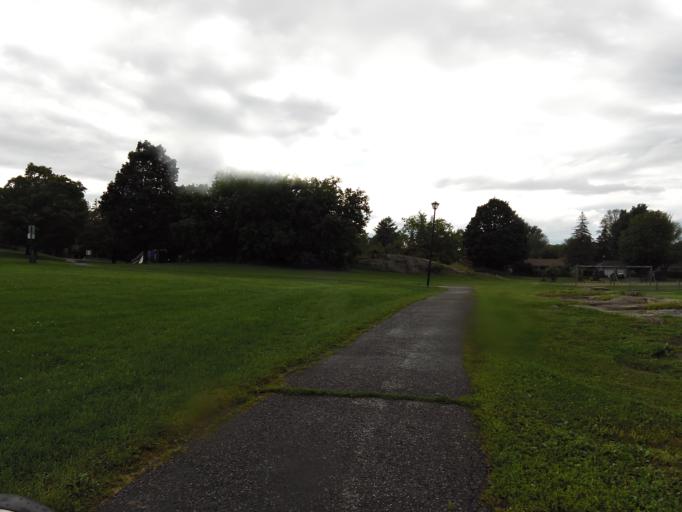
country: CA
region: Ontario
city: Bells Corners
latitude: 45.3319
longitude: -75.9099
